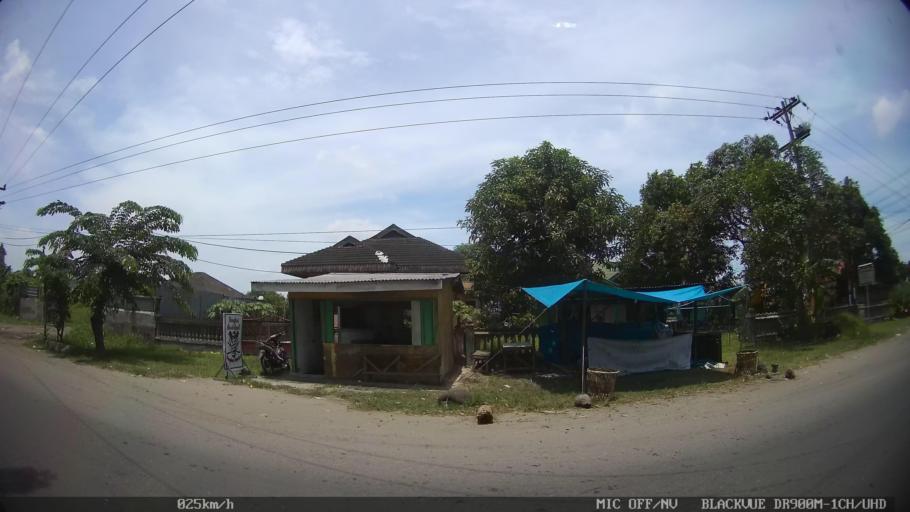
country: ID
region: North Sumatra
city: Belawan
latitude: 3.7523
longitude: 98.6761
